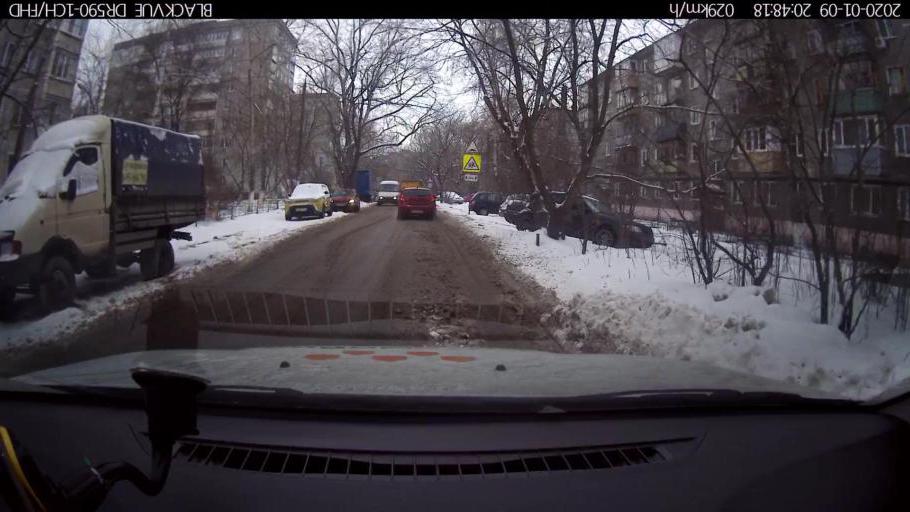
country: RU
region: Nizjnij Novgorod
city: Nizhniy Novgorod
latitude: 56.2916
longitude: 43.9372
